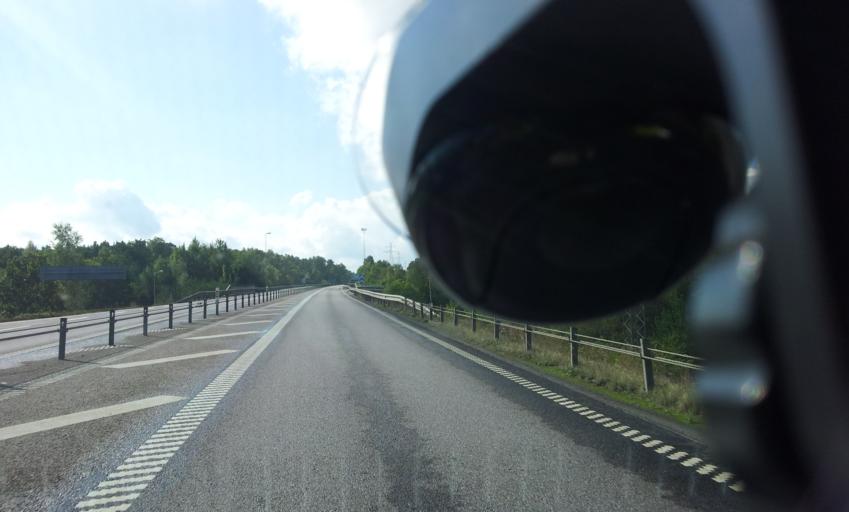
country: SE
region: Kalmar
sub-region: Oskarshamns Kommun
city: Oskarshamn
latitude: 57.2777
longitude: 16.4467
